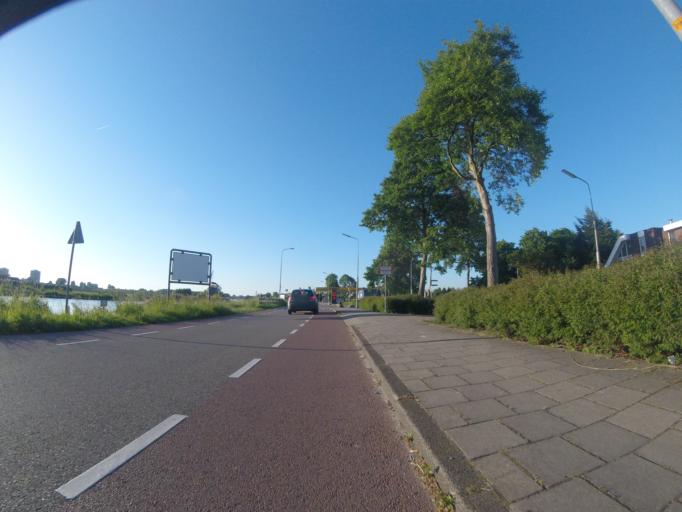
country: NL
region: North Holland
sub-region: Gemeente Haarlem
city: Haarlem
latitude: 52.3545
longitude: 4.6772
